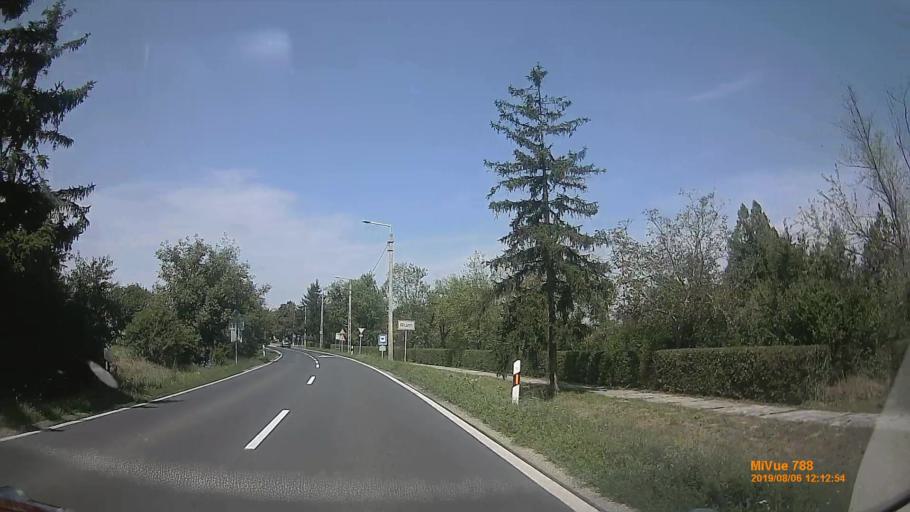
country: HU
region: Vas
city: Vasvar
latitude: 47.1290
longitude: 16.8465
